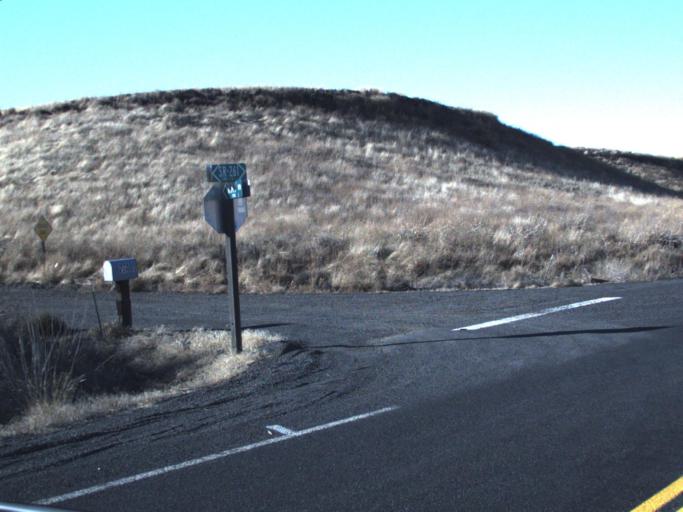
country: US
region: Washington
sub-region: Adams County
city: Ritzville
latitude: 46.8260
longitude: -118.3241
